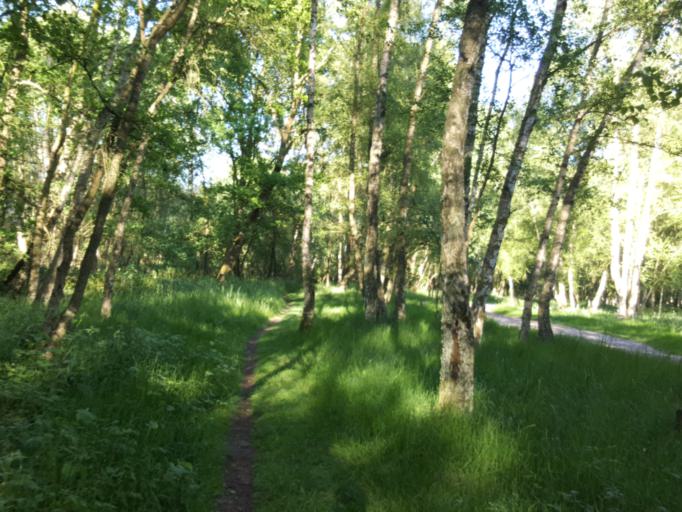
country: DE
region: Schleswig-Holstein
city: Oststeinbek
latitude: 53.5196
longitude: 10.1369
